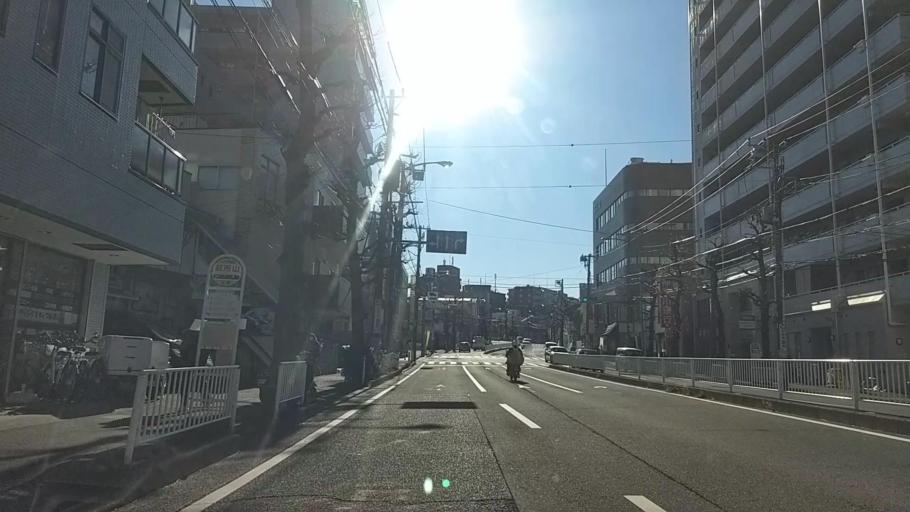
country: JP
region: Kanagawa
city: Yokohama
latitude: 35.4557
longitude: 139.6188
